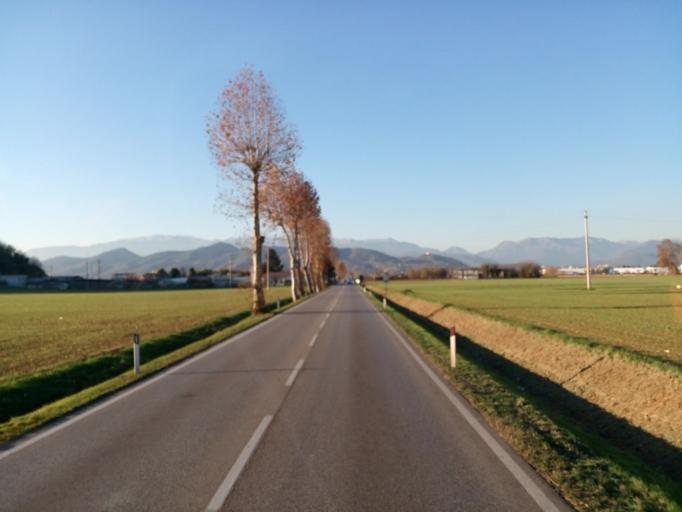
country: IT
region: Veneto
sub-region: Provincia di Treviso
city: Crocetta-Nogare
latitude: 45.8036
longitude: 12.0289
